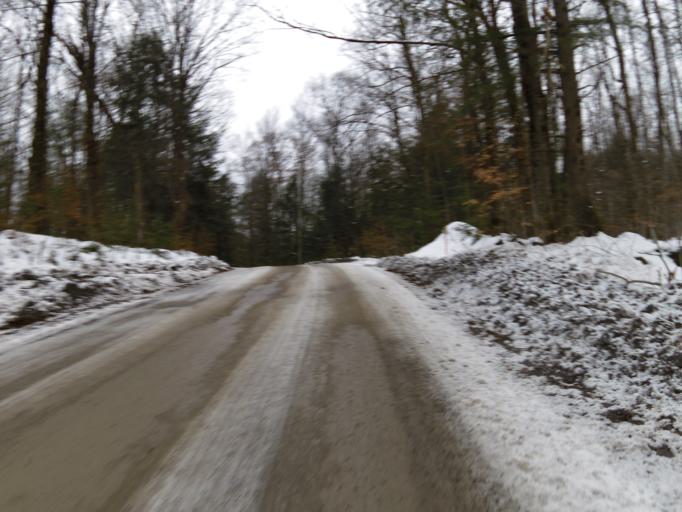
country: CA
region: Ontario
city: Carleton Place
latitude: 45.1829
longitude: -76.2246
